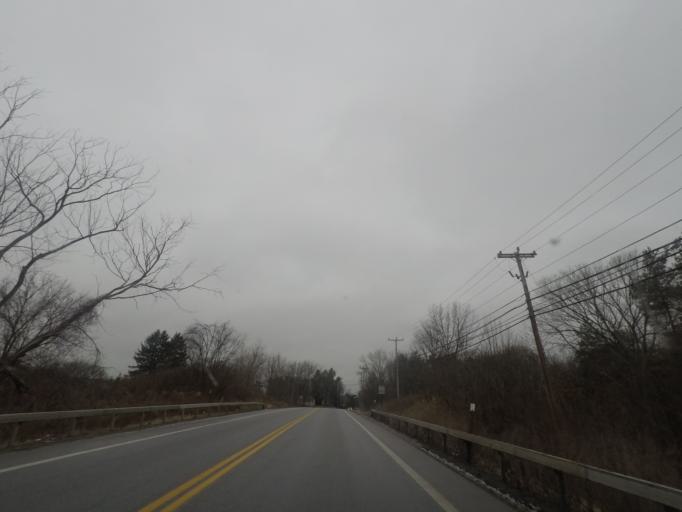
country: US
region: New York
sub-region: Saratoga County
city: Mechanicville
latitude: 42.8994
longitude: -73.7090
